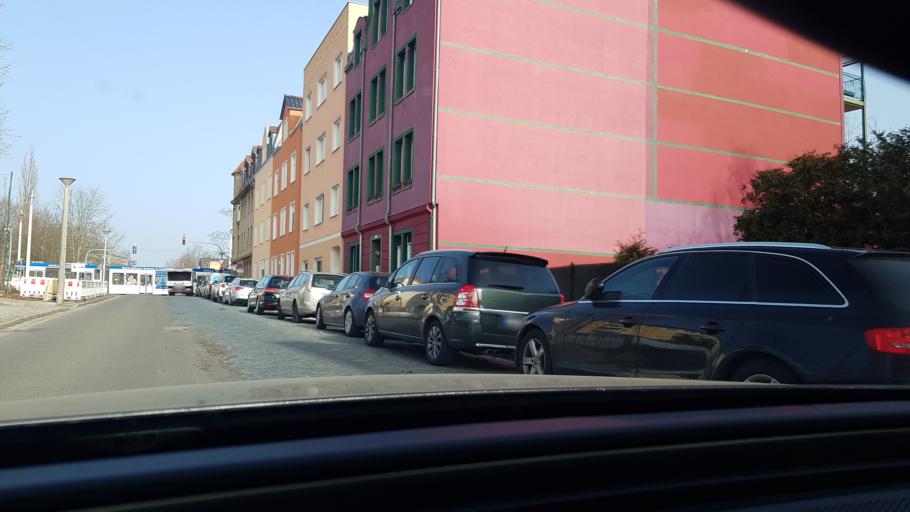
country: DE
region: Brandenburg
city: Cottbus
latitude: 51.7559
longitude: 14.3099
